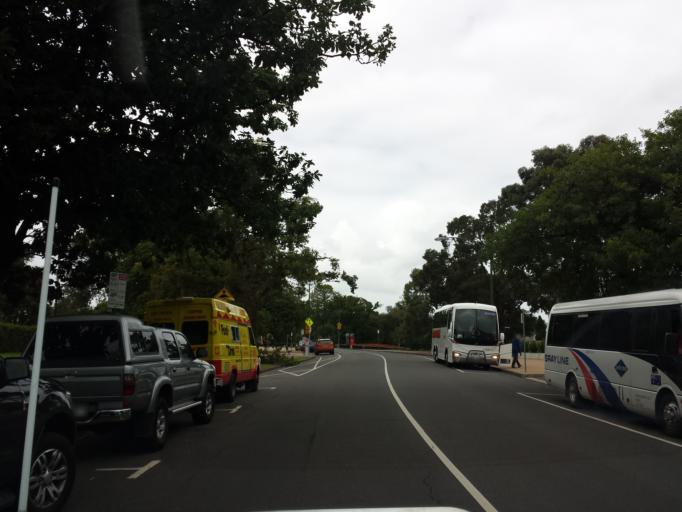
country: AU
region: Victoria
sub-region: Port Phillip
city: South Melbourne
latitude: -37.8292
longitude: 144.9741
